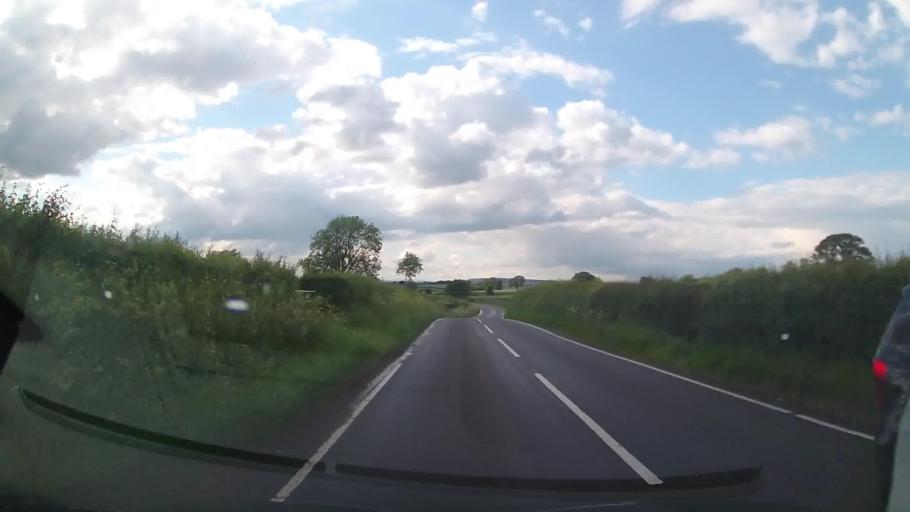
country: GB
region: England
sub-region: Shropshire
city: Withington
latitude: 52.6615
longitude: -2.6202
